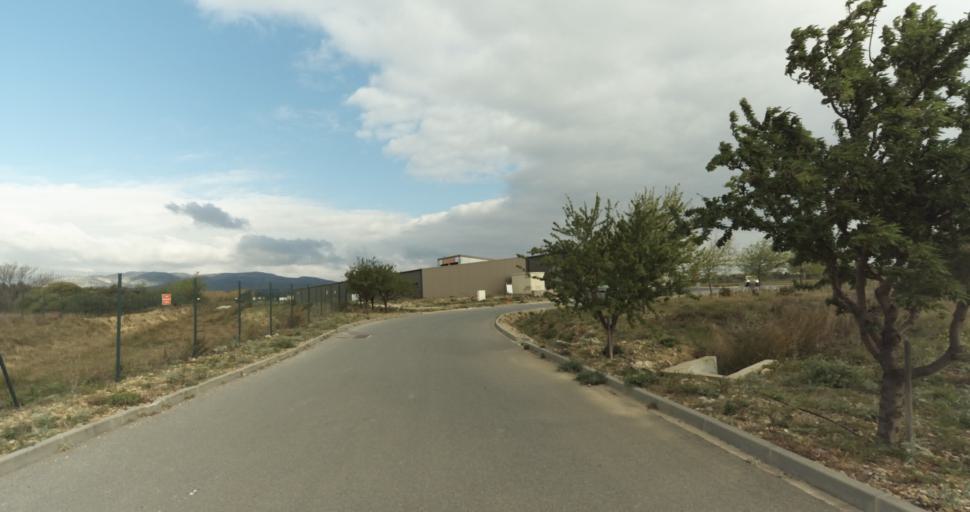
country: FR
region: Languedoc-Roussillon
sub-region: Departement de l'Aude
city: Leucate
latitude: 42.9327
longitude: 2.9962
